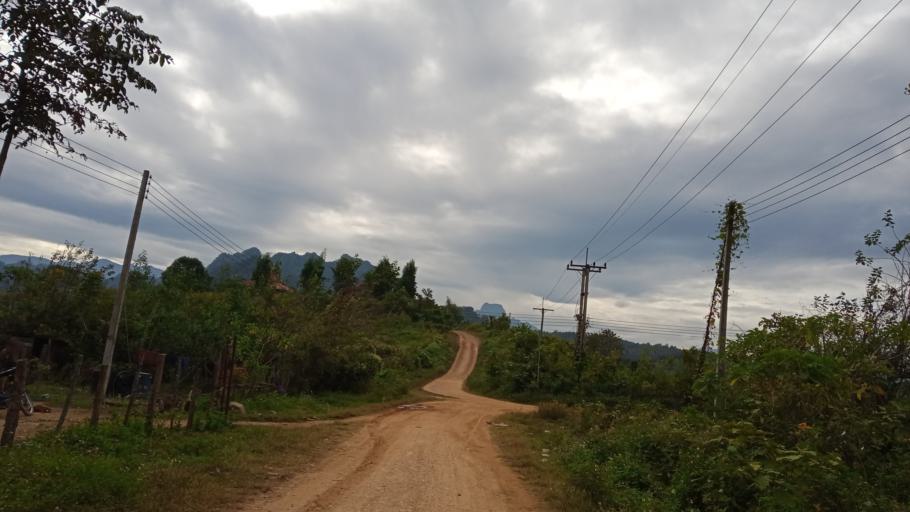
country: LA
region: Xiangkhoang
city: Phonsavan
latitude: 19.1083
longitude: 102.9278
